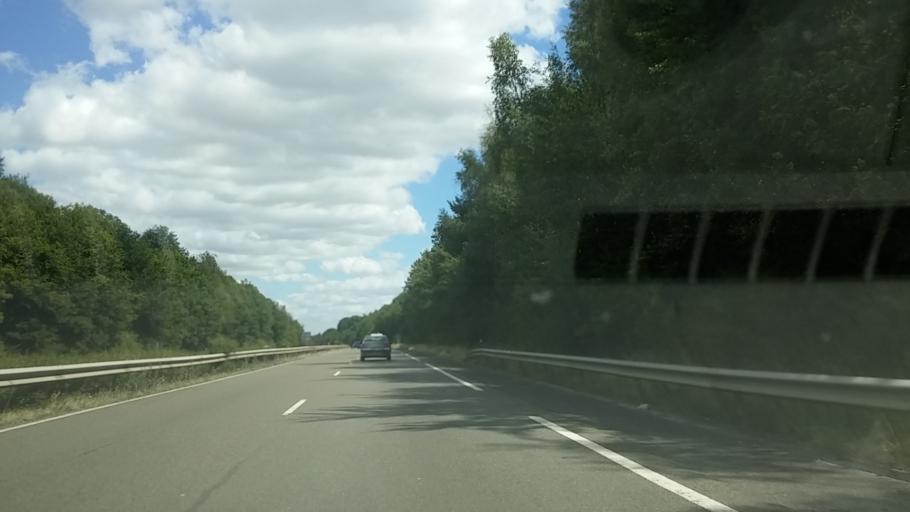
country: FR
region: Ile-de-France
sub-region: Departement des Yvelines
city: La Queue-les-Yvelines
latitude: 48.7983
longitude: 1.7518
